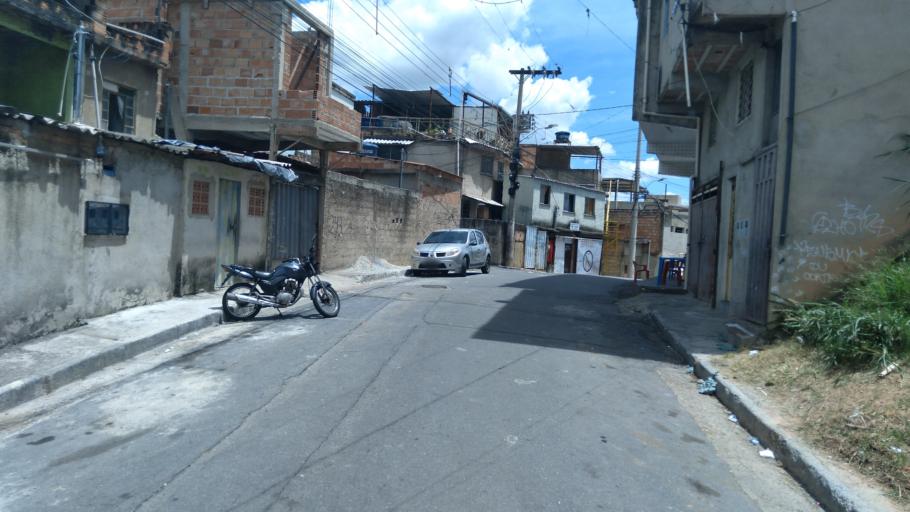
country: BR
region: Minas Gerais
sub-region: Contagem
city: Contagem
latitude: -19.9173
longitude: -44.0087
